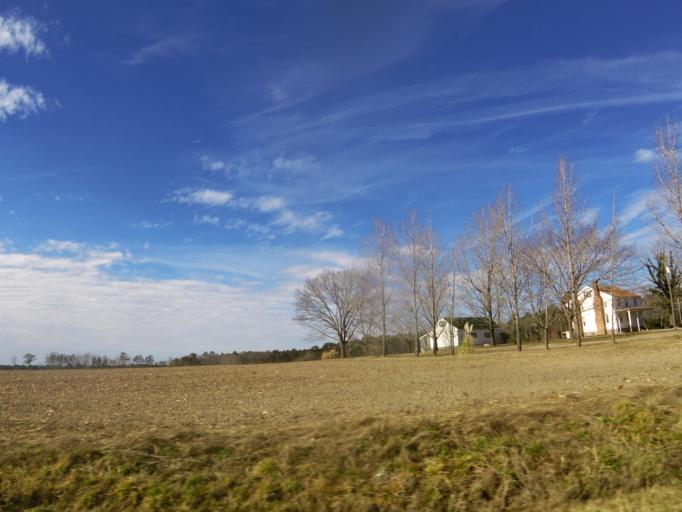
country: US
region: Virginia
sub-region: City of Franklin
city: Franklin
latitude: 36.7569
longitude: -76.8615
